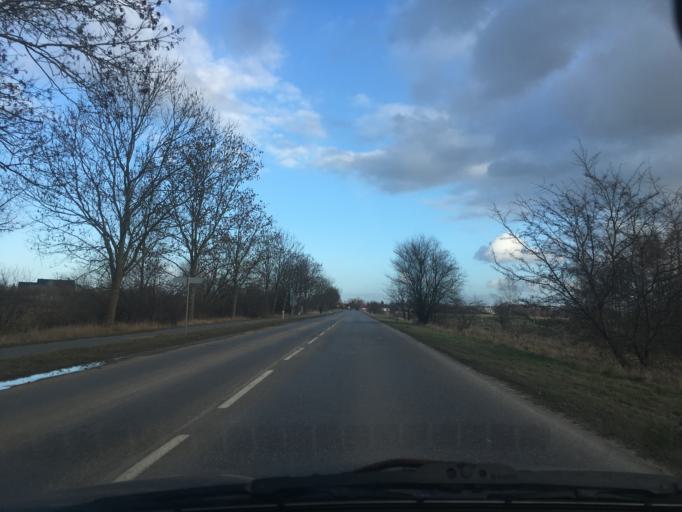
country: PL
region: Pomeranian Voivodeship
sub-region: Powiat gdanski
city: Cedry Wielkie
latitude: 54.3297
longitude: 18.7900
